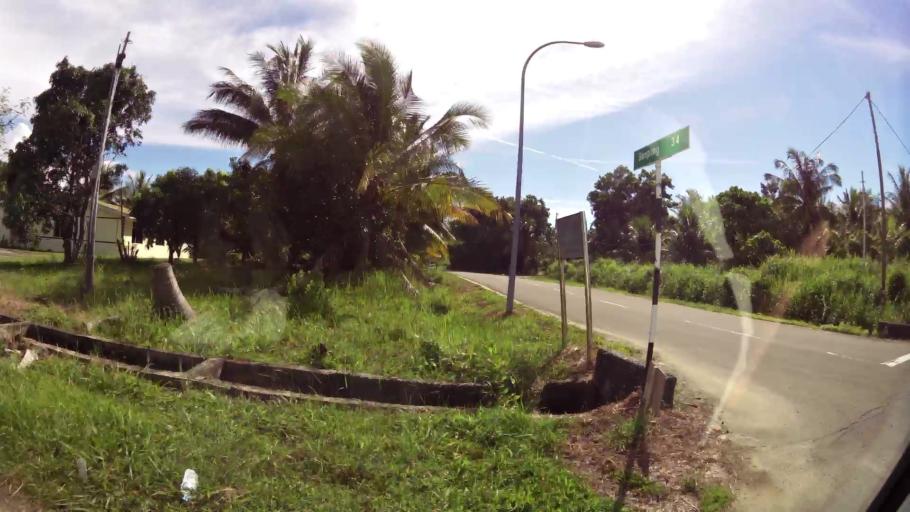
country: BN
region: Brunei and Muara
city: Bandar Seri Begawan
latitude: 5.0223
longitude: 115.0461
